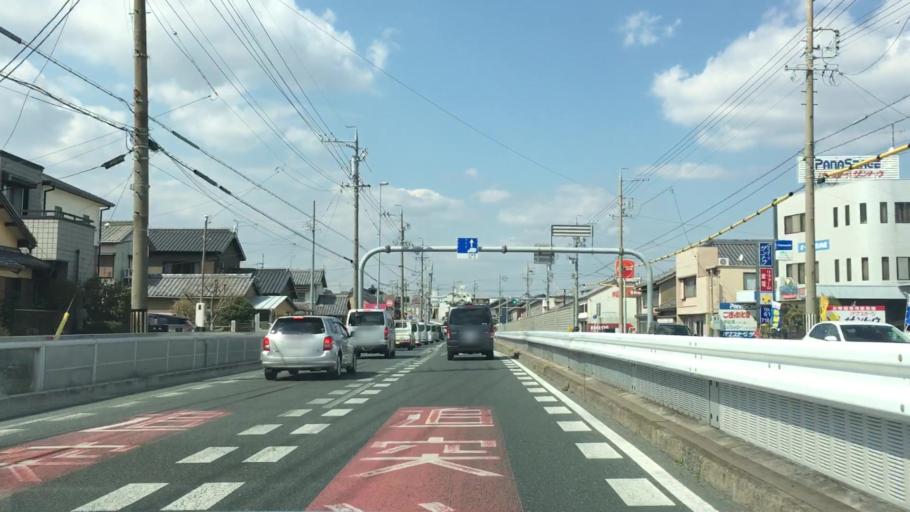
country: JP
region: Aichi
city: Toyohashi
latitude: 34.7569
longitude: 137.4095
